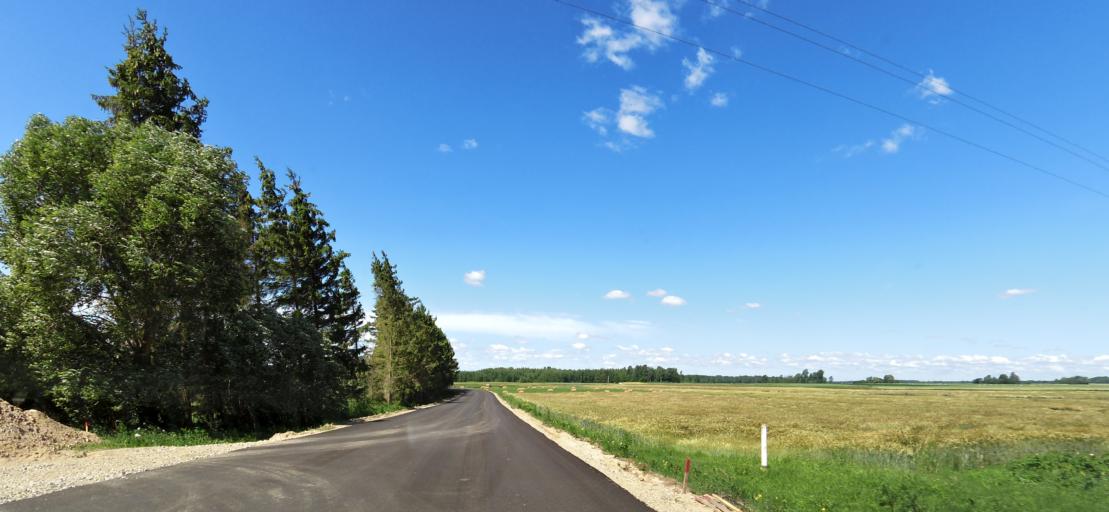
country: LT
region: Panevezys
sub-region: Birzai
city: Birzai
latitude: 56.3001
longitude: 24.6210
